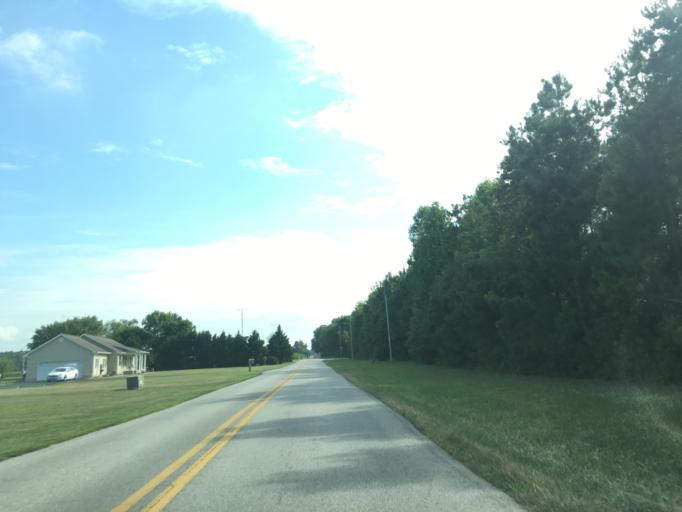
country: US
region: Delaware
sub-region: Sussex County
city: Bridgeville
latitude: 38.7603
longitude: -75.4970
